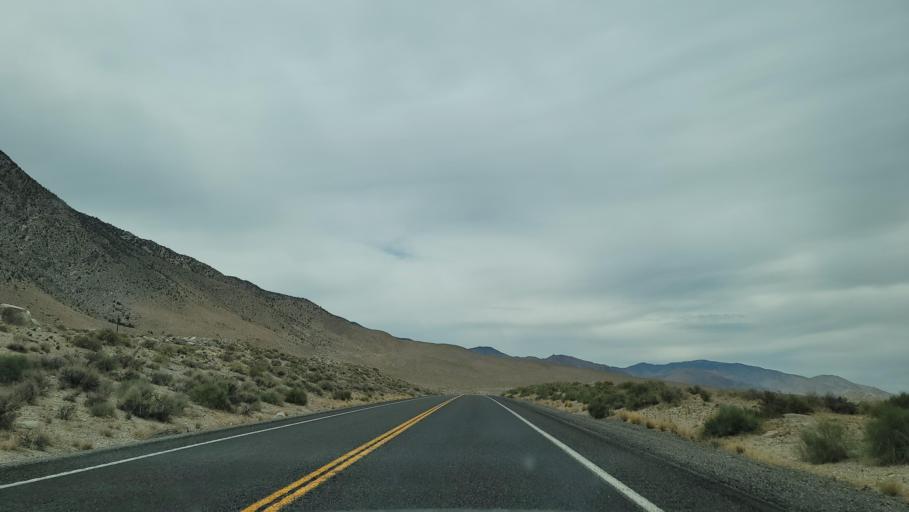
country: US
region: Nevada
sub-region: Mineral County
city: Hawthorne
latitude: 38.5784
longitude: -118.7012
